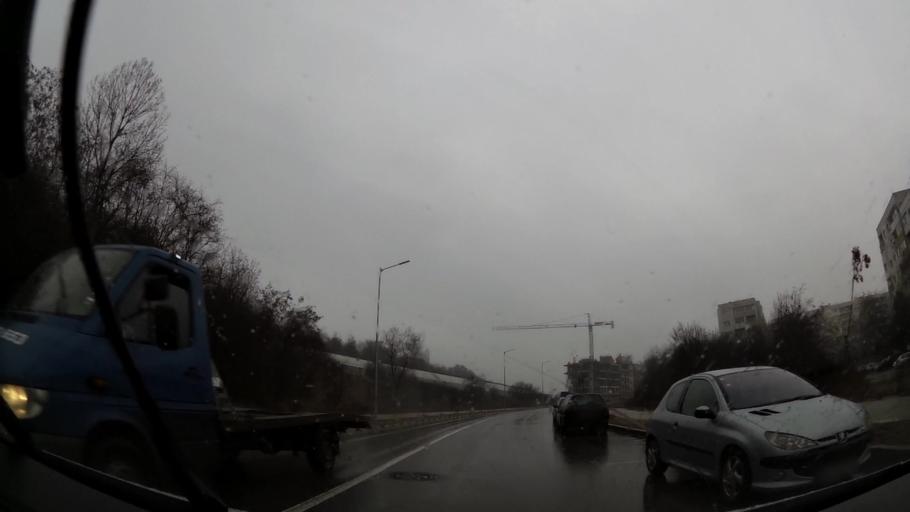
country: BG
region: Sofia-Capital
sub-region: Stolichna Obshtina
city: Sofia
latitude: 42.6520
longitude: 23.3960
